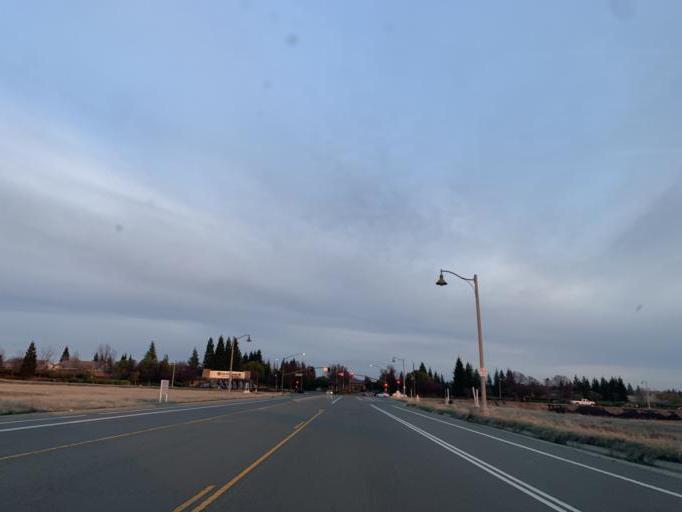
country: US
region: California
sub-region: Placer County
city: Lincoln
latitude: 38.8548
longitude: -121.2865
